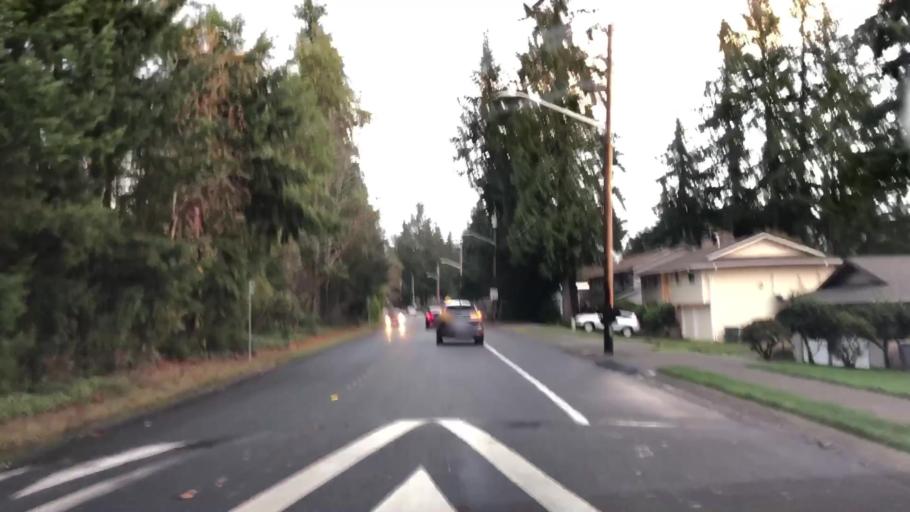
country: US
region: Washington
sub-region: King County
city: Eastgate
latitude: 47.5834
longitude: -122.1255
